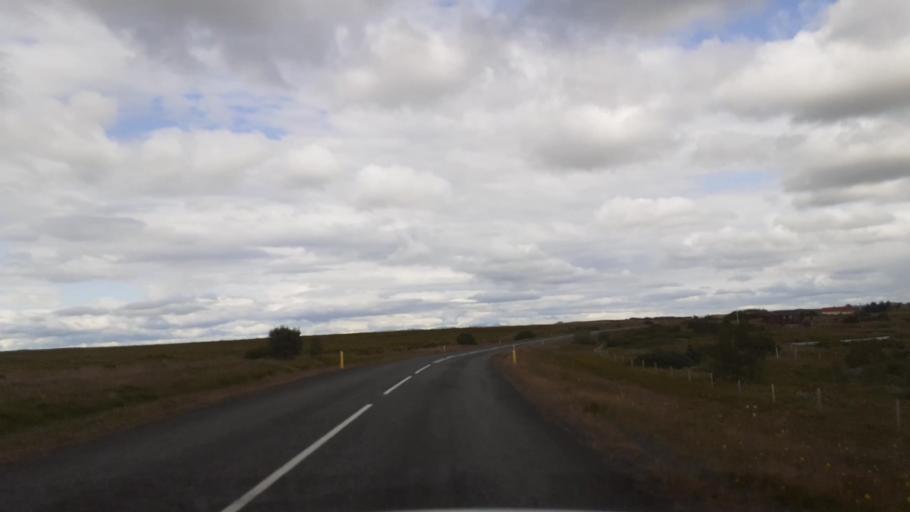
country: IS
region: South
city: Vestmannaeyjar
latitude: 63.8248
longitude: -20.4278
